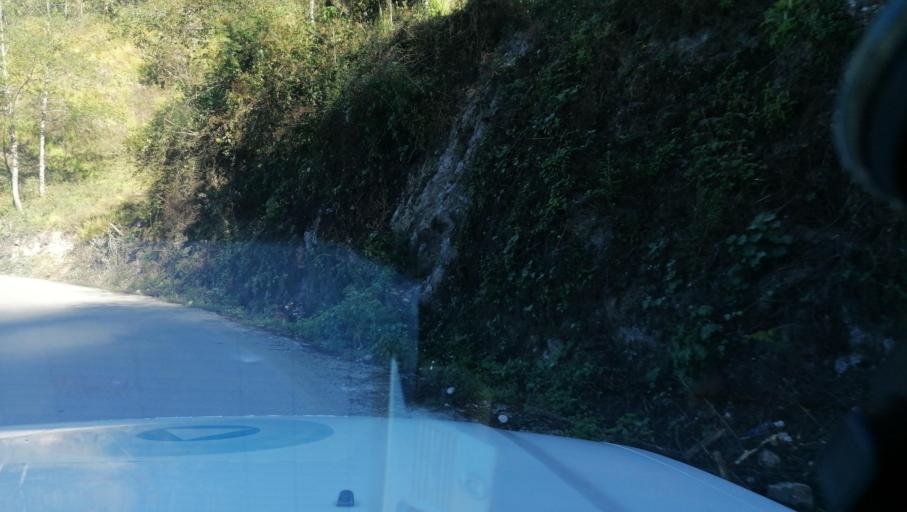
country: MX
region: Chiapas
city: Motozintla de Mendoza
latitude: 15.2731
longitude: -92.2295
